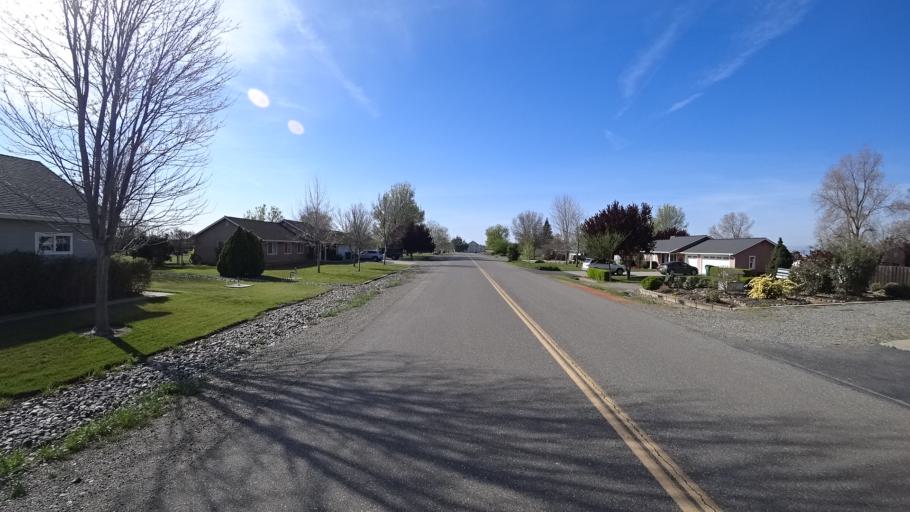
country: US
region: California
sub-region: Glenn County
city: Willows
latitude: 39.6132
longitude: -122.1953
